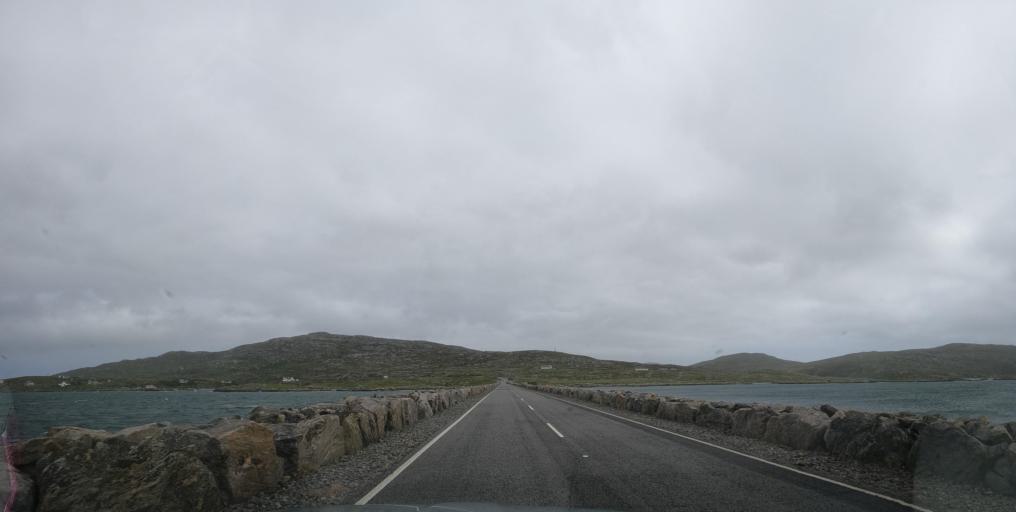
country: GB
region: Scotland
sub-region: Eilean Siar
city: Isle of South Uist
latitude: 57.0995
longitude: -7.3176
